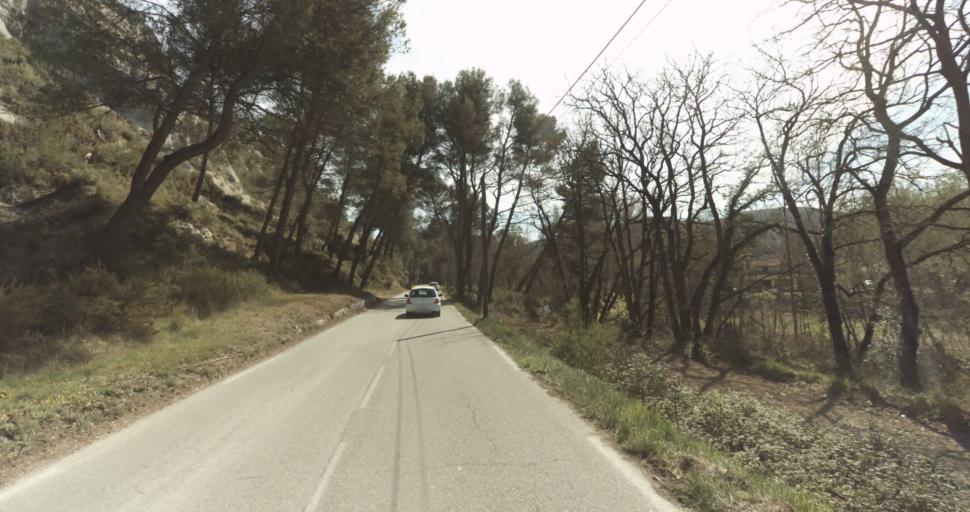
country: FR
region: Provence-Alpes-Cote d'Azur
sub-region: Departement des Bouches-du-Rhone
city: Ventabren
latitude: 43.5249
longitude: 5.2932
